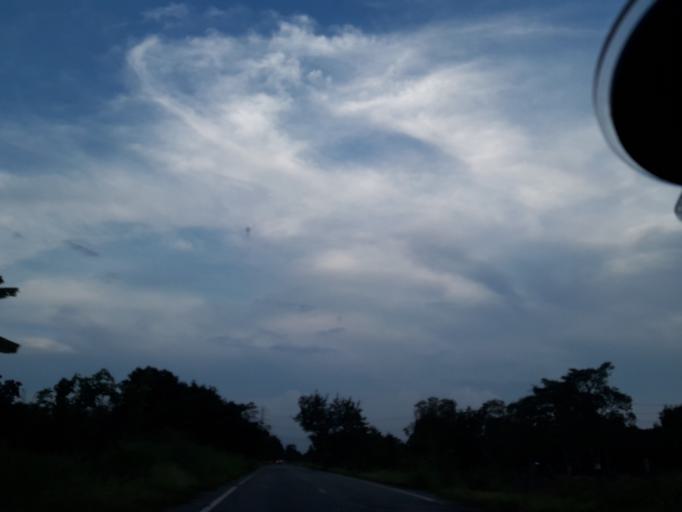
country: TH
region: Pathum Thani
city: Nong Suea
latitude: 14.1912
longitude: 100.8689
